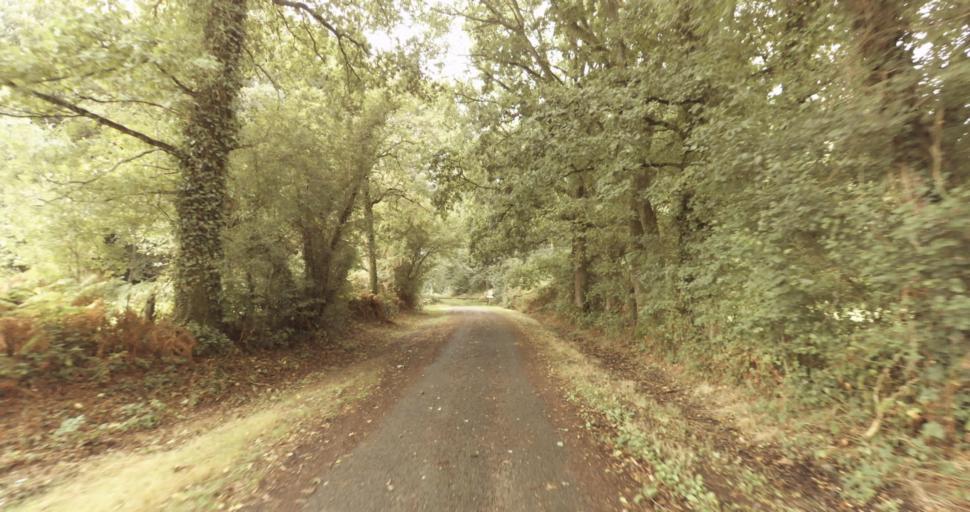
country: FR
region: Lower Normandy
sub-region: Departement de l'Orne
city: Sainte-Gauburge-Sainte-Colombe
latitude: 48.7077
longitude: 0.4792
